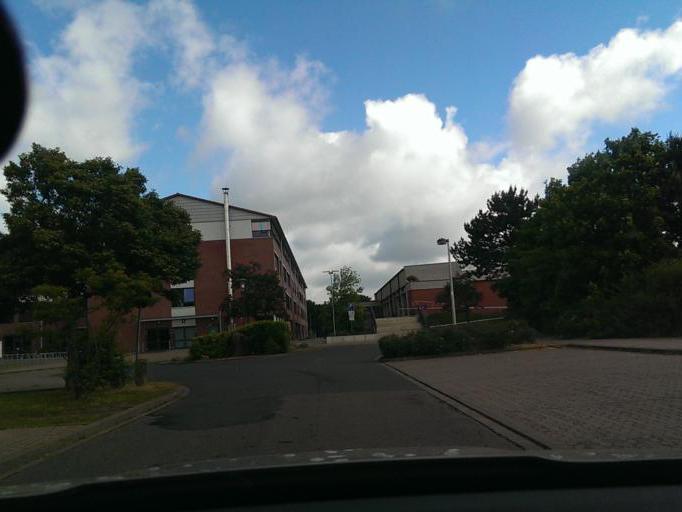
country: DE
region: Lower Saxony
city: Elze
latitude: 52.5487
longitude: 9.7359
